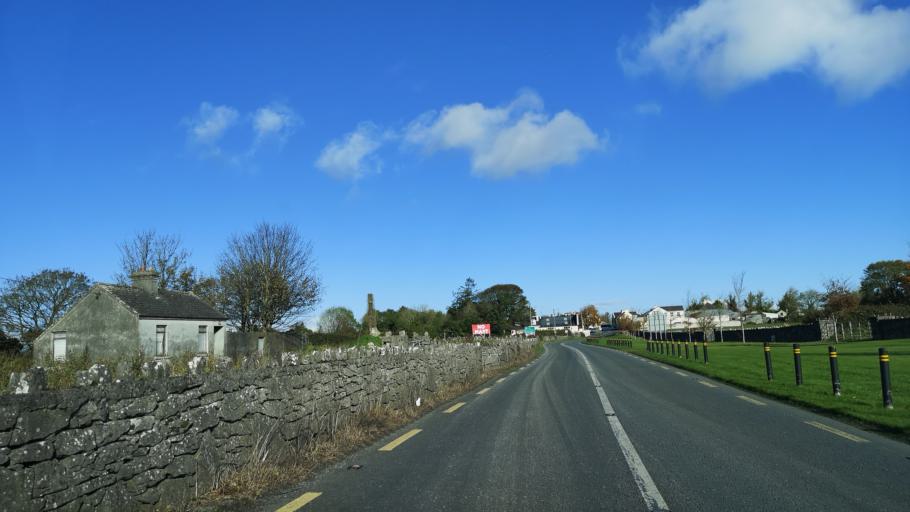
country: IE
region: Connaught
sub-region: Maigh Eo
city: Ballinrobe
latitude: 53.5769
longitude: -9.1225
